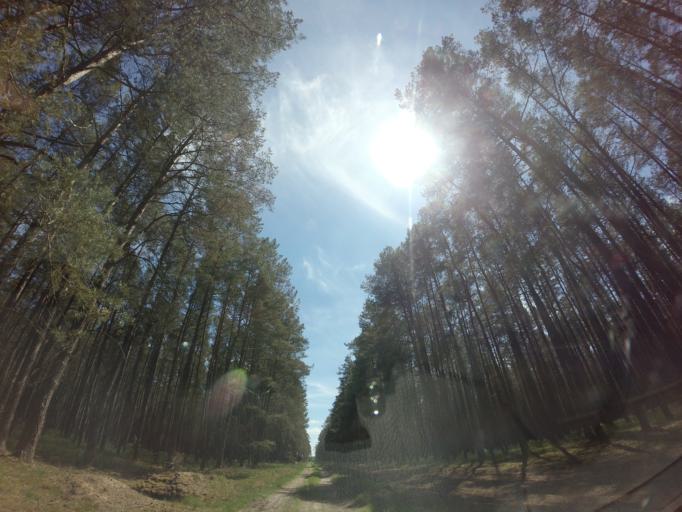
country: PL
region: West Pomeranian Voivodeship
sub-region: Powiat drawski
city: Kalisz Pomorski
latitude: 53.1782
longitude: 15.9011
